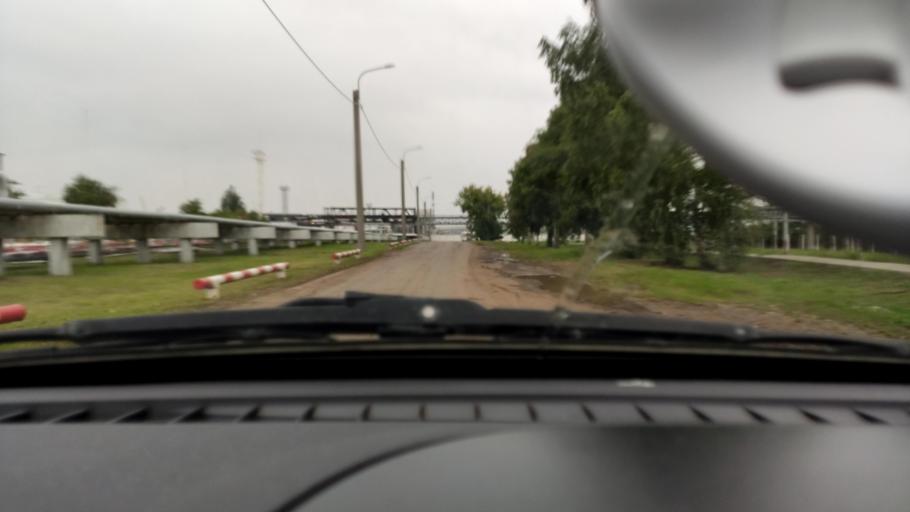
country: RU
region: Perm
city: Gamovo
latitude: 57.9088
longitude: 56.1488
